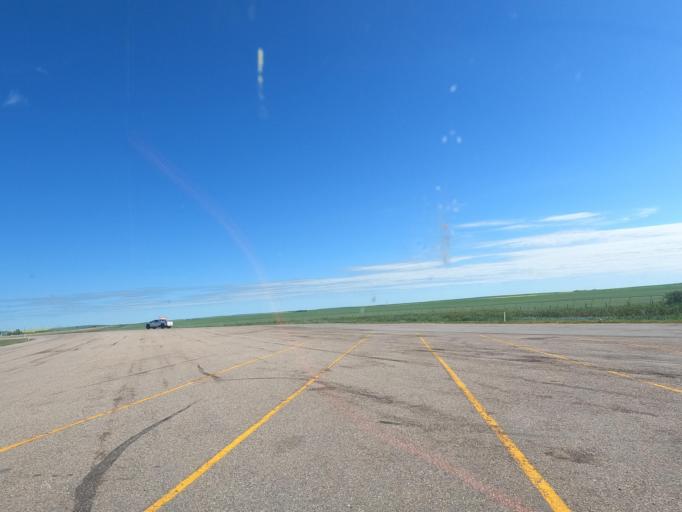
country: CA
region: Alberta
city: Strathmore
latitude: 50.9873
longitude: -113.0731
